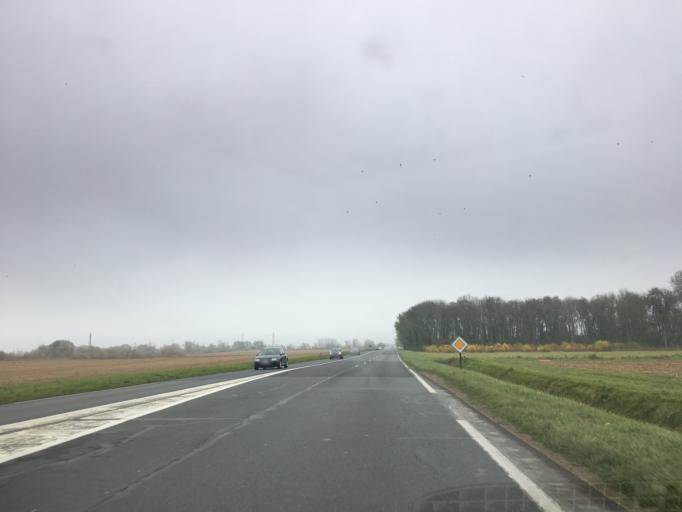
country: FR
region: Ile-de-France
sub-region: Departement de Seine-et-Marne
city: Varennes-sur-Seine
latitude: 48.3609
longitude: 2.9326
